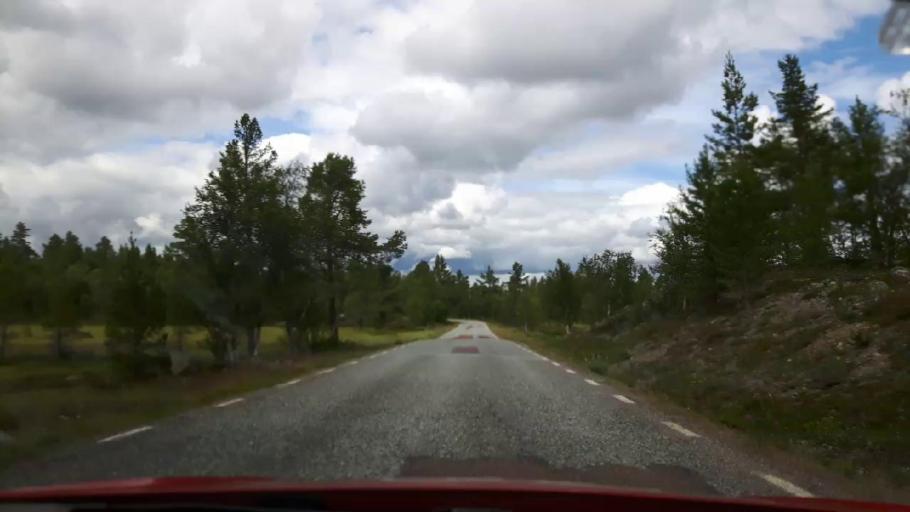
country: NO
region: Hedmark
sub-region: Trysil
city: Innbygda
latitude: 62.1145
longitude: 12.9756
